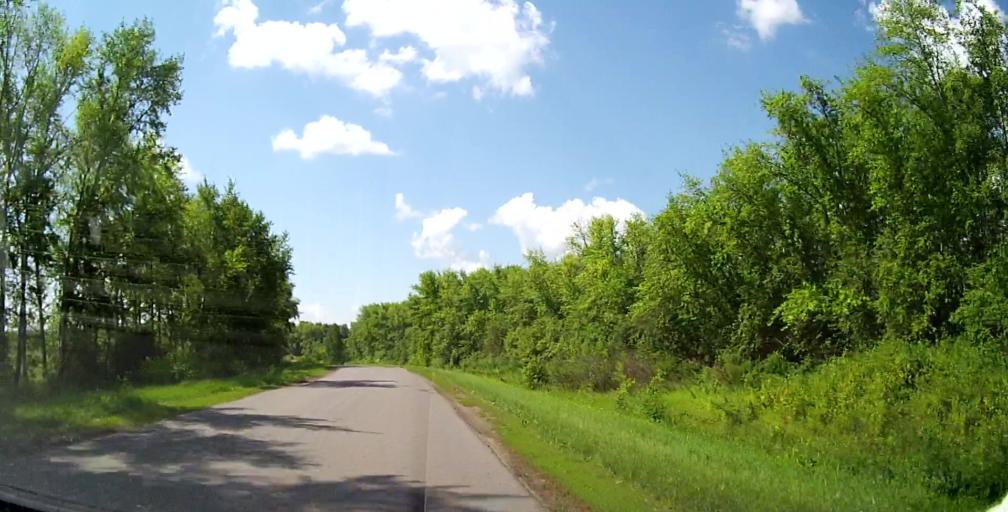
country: RU
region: Lipetsk
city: Chaplygin
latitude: 53.3076
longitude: 39.9537
